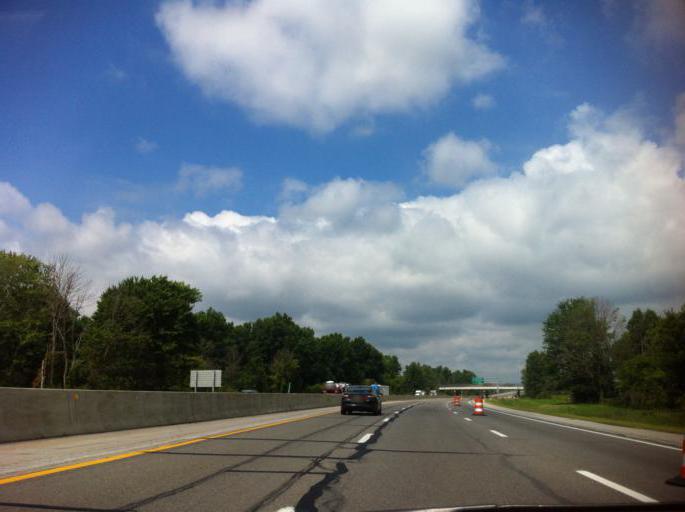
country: US
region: Ohio
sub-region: Lorain County
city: North Ridgeville
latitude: 41.3695
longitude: -81.9715
